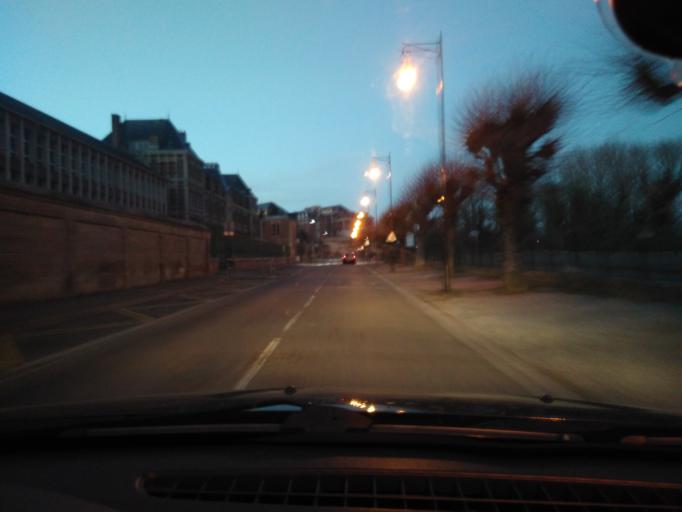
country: FR
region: Picardie
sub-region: Departement de l'Aisne
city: Laon
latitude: 49.5582
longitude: 3.6127
